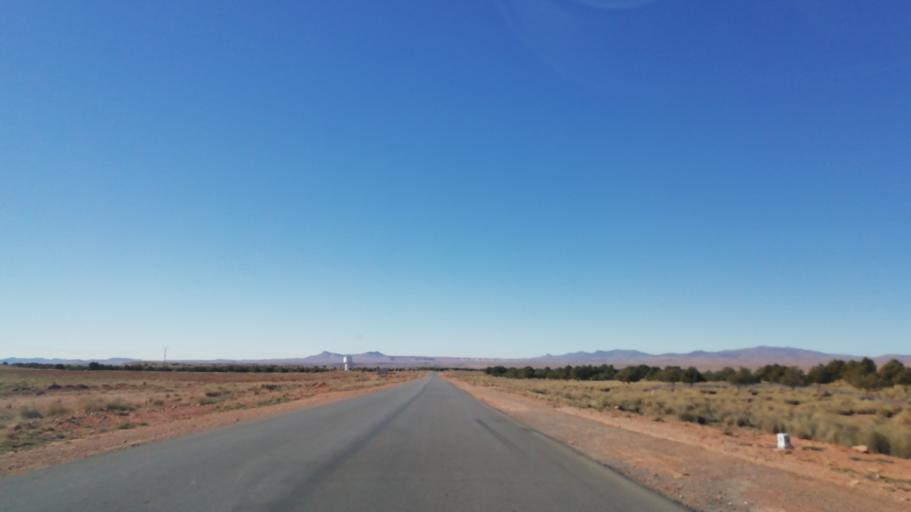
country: DZ
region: El Bayadh
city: El Bayadh
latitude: 33.6333
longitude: 1.3712
